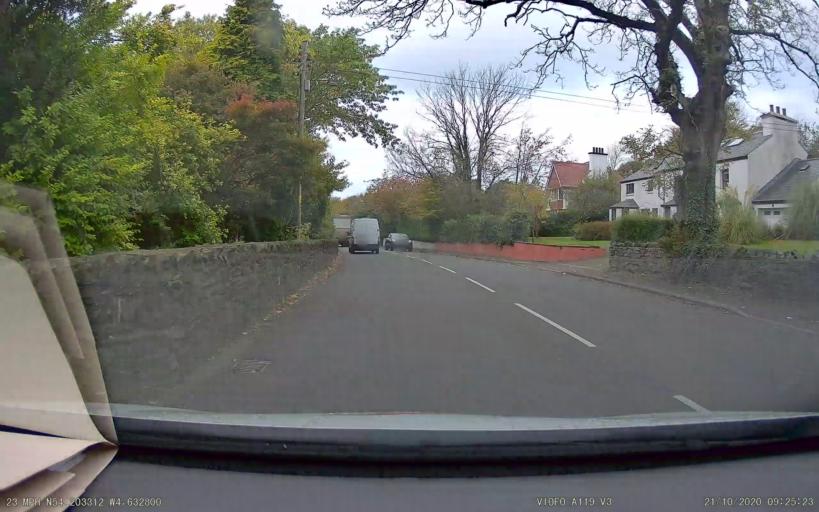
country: IM
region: Castletown
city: Castletown
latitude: 54.2033
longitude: -4.6325
